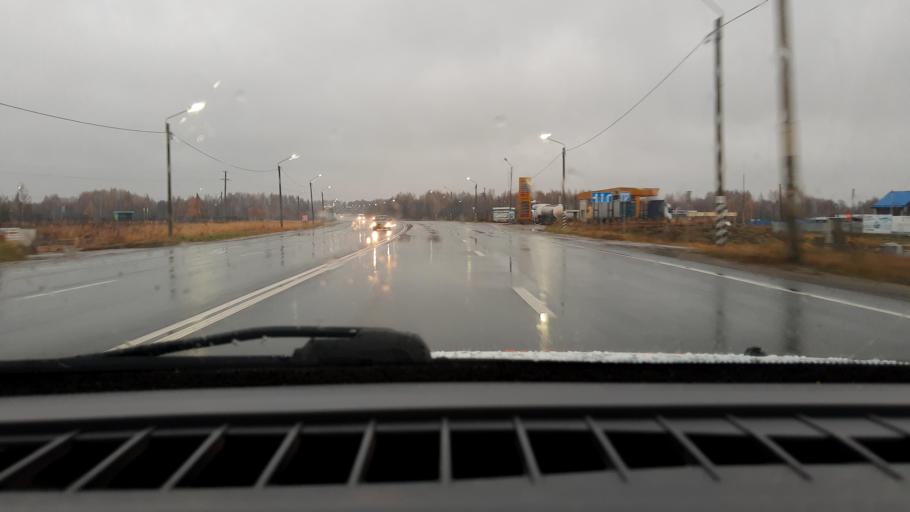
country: RU
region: Nizjnij Novgorod
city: Sitniki
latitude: 56.4998
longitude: 44.0254
